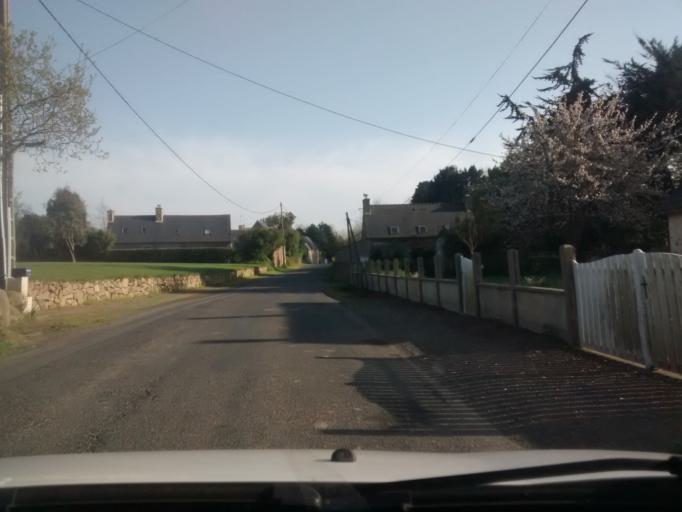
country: FR
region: Brittany
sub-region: Departement des Cotes-d'Armor
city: Penvenan
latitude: 48.8250
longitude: -3.2829
